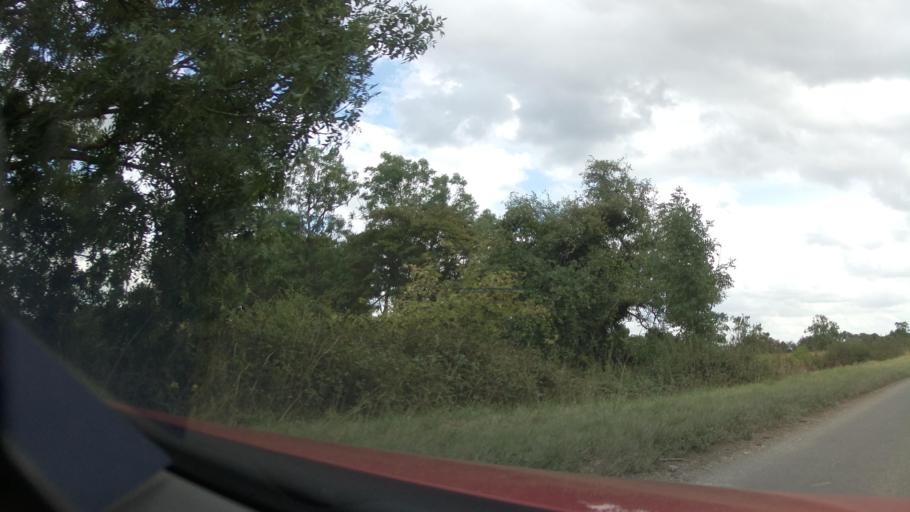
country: GB
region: England
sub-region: North Yorkshire
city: Ripon
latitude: 54.1763
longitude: -1.5535
